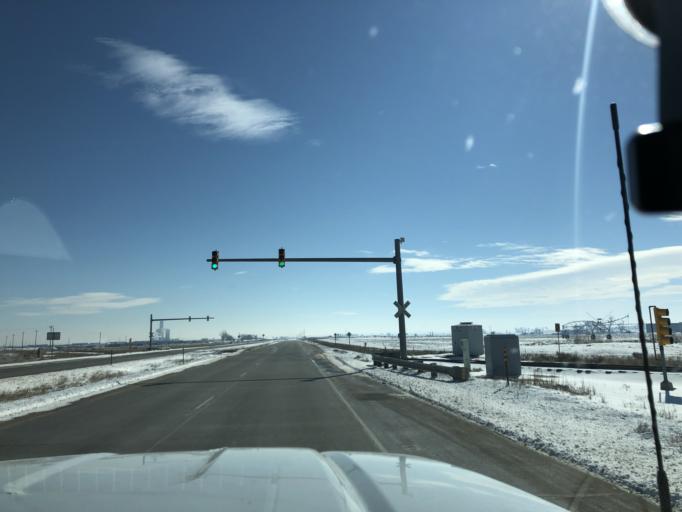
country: US
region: Colorado
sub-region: Weld County
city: Kersey
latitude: 40.3847
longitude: -104.5305
